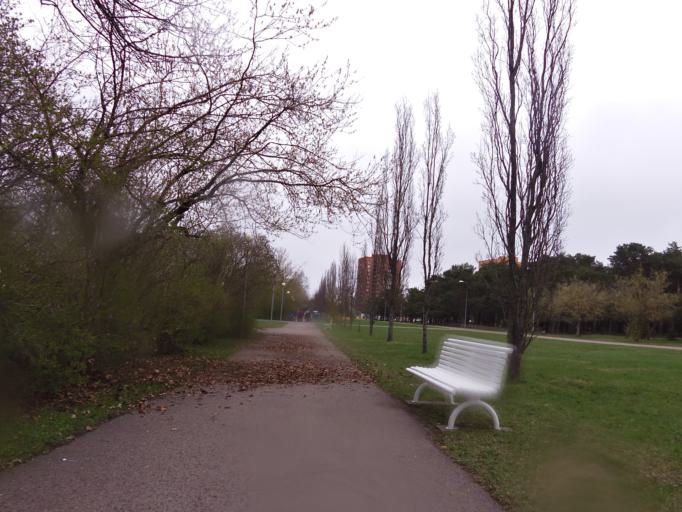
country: EE
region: Harju
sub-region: Tallinna linn
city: Tallinn
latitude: 59.4397
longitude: 24.6849
